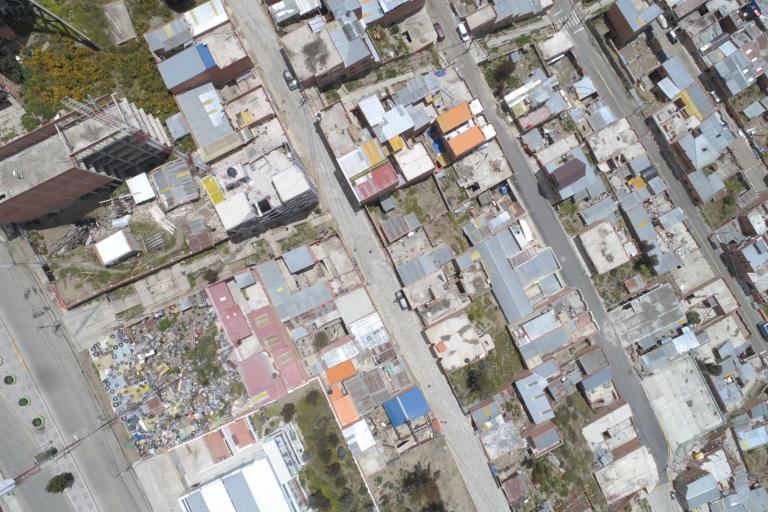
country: BO
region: La Paz
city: La Paz
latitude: -16.5253
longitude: -68.1463
